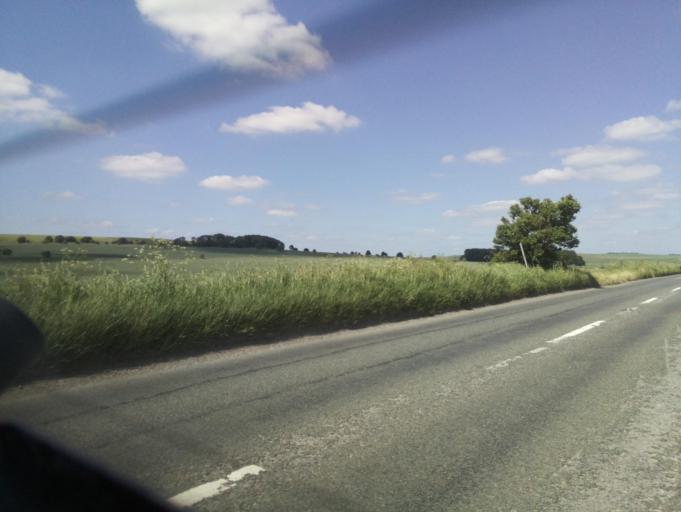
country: GB
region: England
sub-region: Wiltshire
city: Devizes
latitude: 51.3912
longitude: -1.9420
